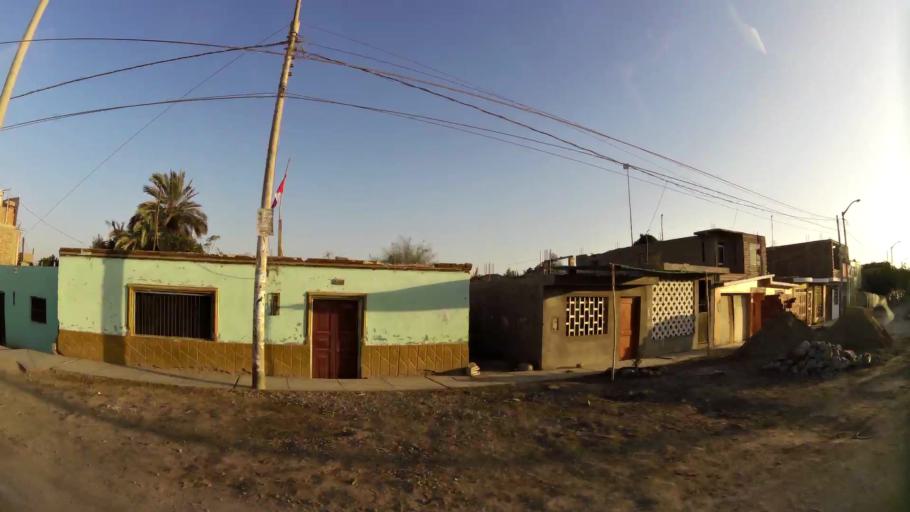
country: PE
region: Ica
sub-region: Provincia de Pisco
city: Villa Tupac Amaru
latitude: -13.7021
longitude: -76.1549
